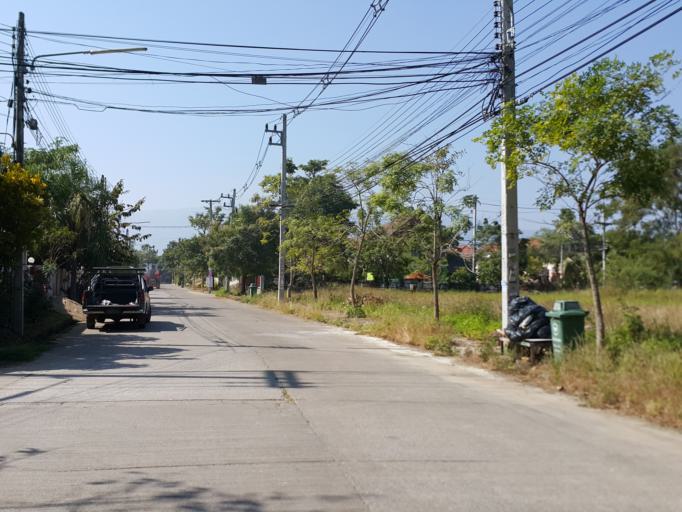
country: TH
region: Chiang Mai
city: Chiang Mai
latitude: 18.8277
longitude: 99.0046
